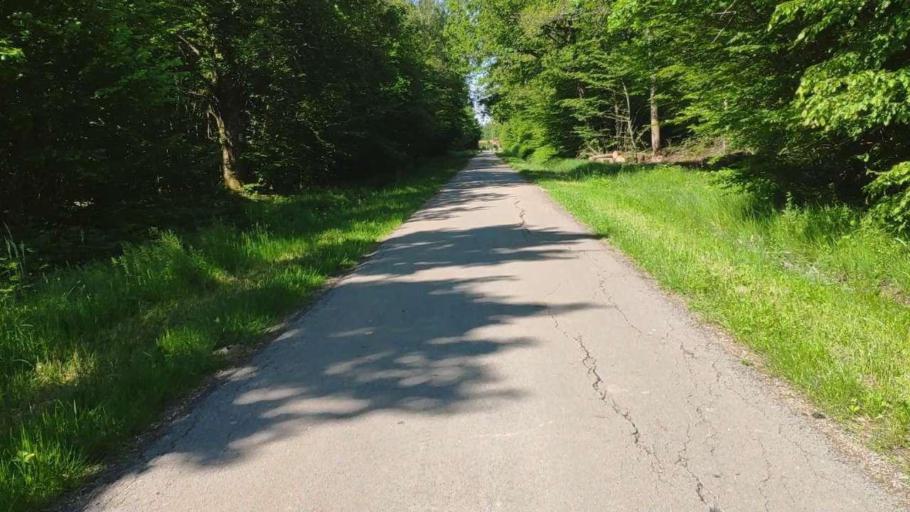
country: FR
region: Franche-Comte
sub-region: Departement du Jura
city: Bletterans
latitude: 46.7910
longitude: 5.4451
